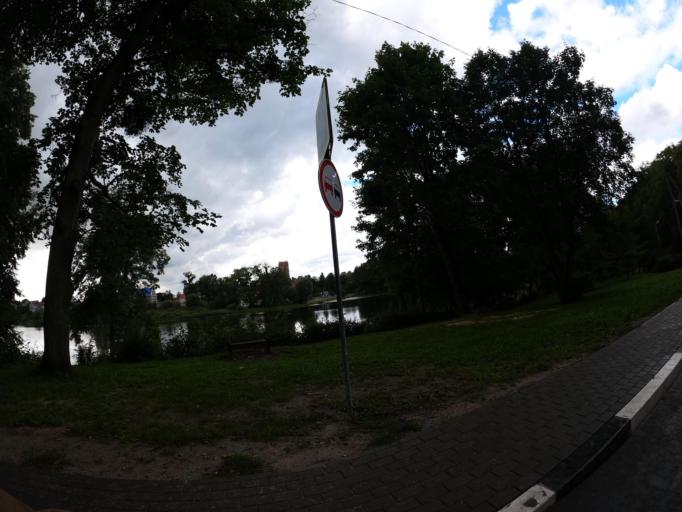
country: RU
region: Kaliningrad
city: Zheleznodorozhnyy
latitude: 54.3628
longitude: 21.3106
